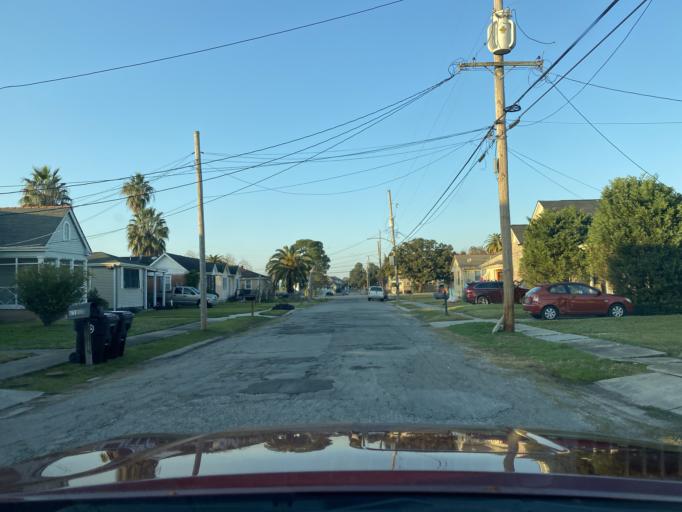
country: US
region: Louisiana
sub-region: Orleans Parish
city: New Orleans
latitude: 30.0212
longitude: -90.0586
